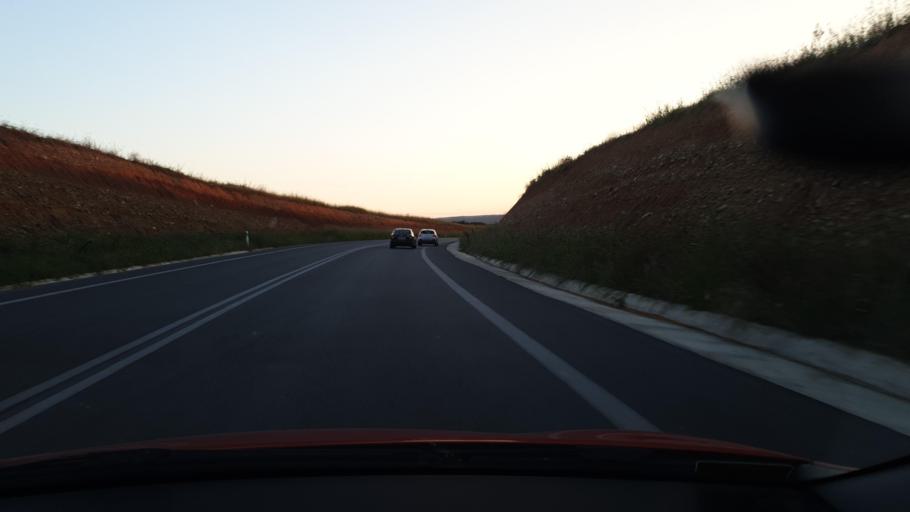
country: GR
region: Central Macedonia
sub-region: Nomos Chalkidikis
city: Galatista
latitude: 40.4638
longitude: 23.2283
